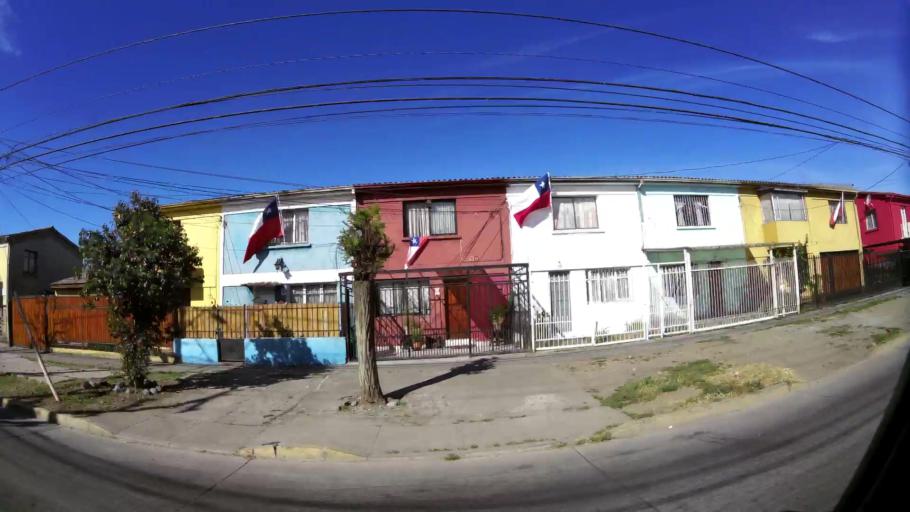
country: CL
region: Santiago Metropolitan
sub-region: Provincia de Santiago
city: Lo Prado
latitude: -33.4614
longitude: -70.7116
